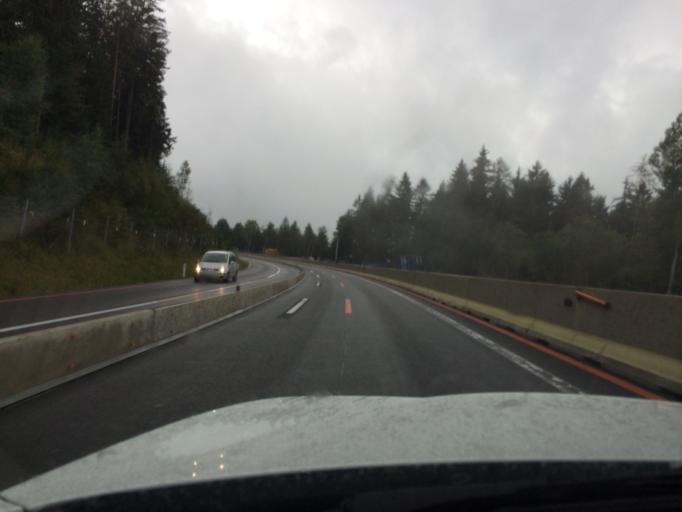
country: AT
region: Styria
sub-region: Politischer Bezirk Voitsberg
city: Voitsberg
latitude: 46.9881
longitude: 15.1241
